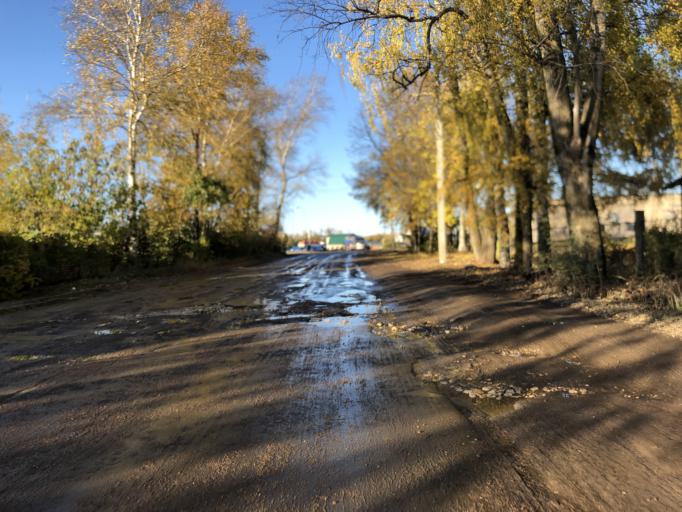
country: RU
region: Tverskaya
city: Rzhev
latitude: 56.2395
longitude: 34.3464
